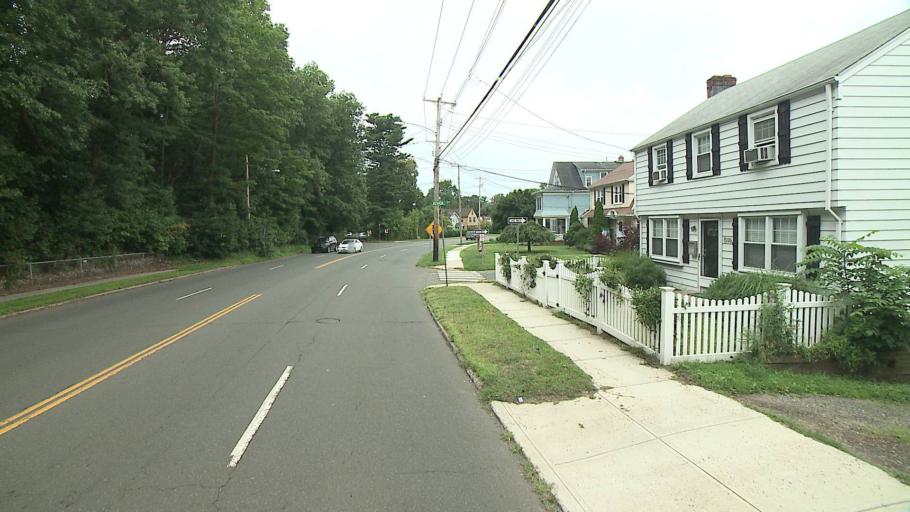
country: US
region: Connecticut
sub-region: New Haven County
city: Hamden
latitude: 41.3577
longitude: -72.9102
